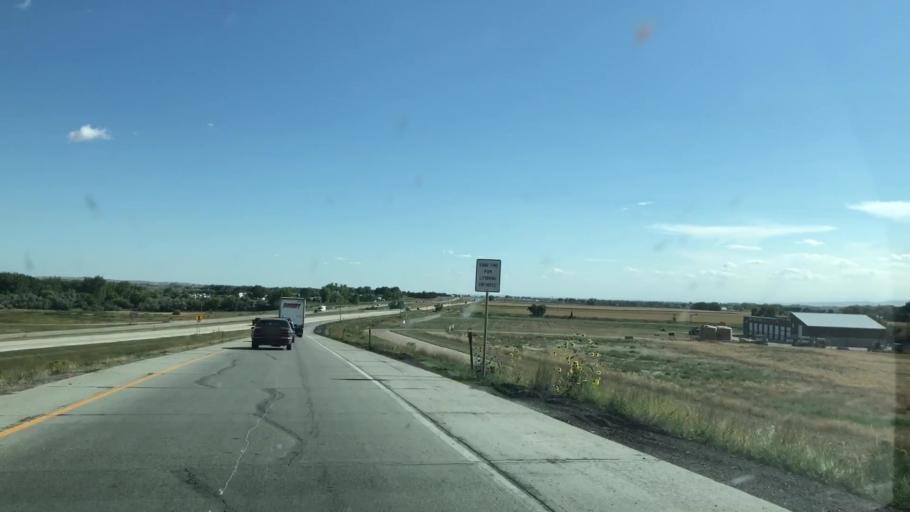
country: US
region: Colorado
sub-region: Larimer County
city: Wellington
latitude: 40.7546
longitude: -104.9933
